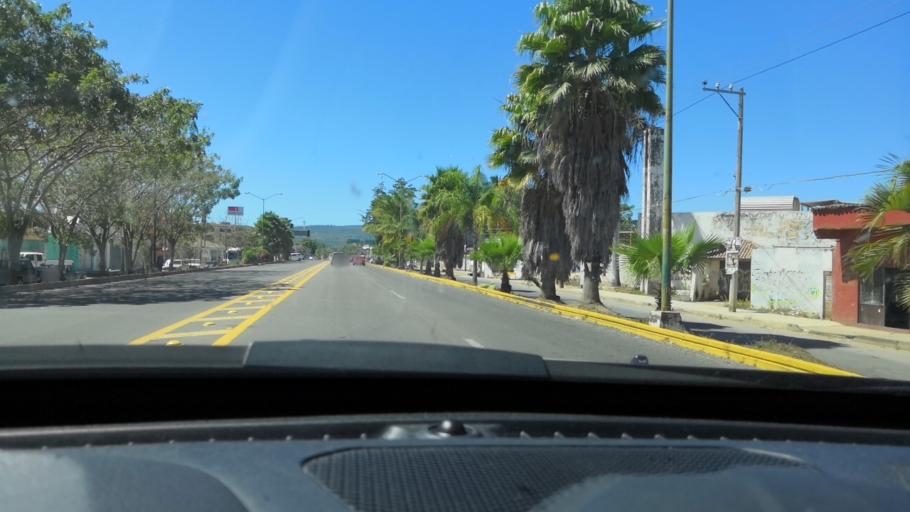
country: MX
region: Nayarit
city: Las Varas
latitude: 21.1806
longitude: -105.1347
